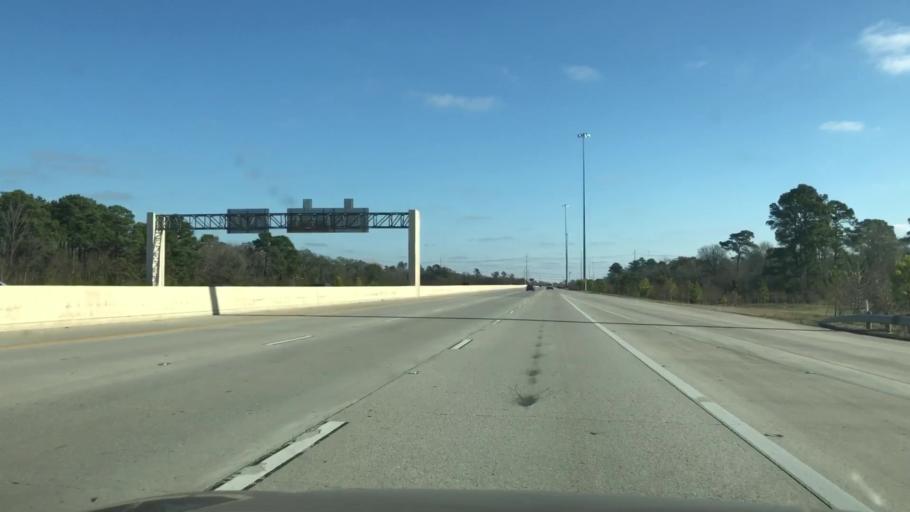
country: US
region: Texas
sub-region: Harris County
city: Jacinto City
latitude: 29.7865
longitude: -95.2433
